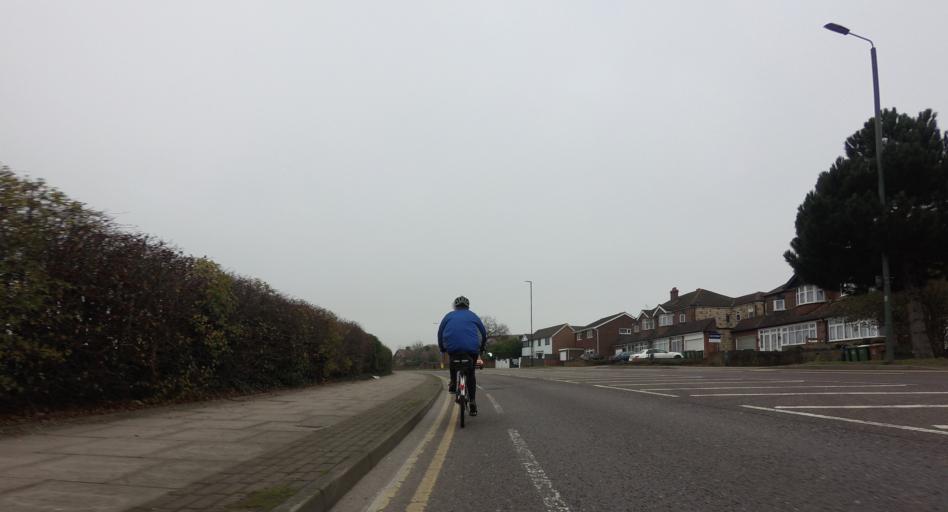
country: GB
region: England
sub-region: Greater London
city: Bexley
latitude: 51.4520
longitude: 0.1522
